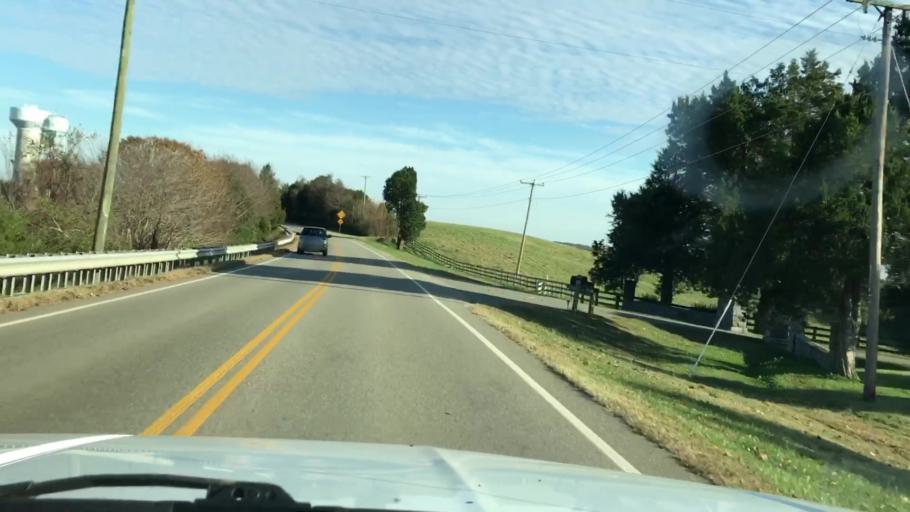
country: US
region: Virginia
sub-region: Goochland County
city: Goochland
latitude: 37.6495
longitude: -77.8406
